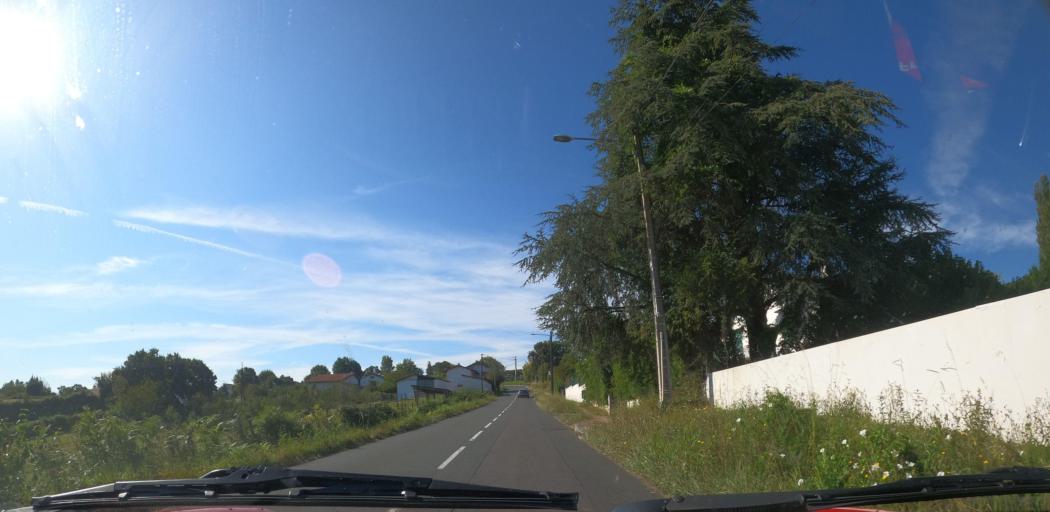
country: FR
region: Aquitaine
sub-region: Departement des Pyrenees-Atlantiques
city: Arbonne
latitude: 43.4127
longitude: -1.5474
